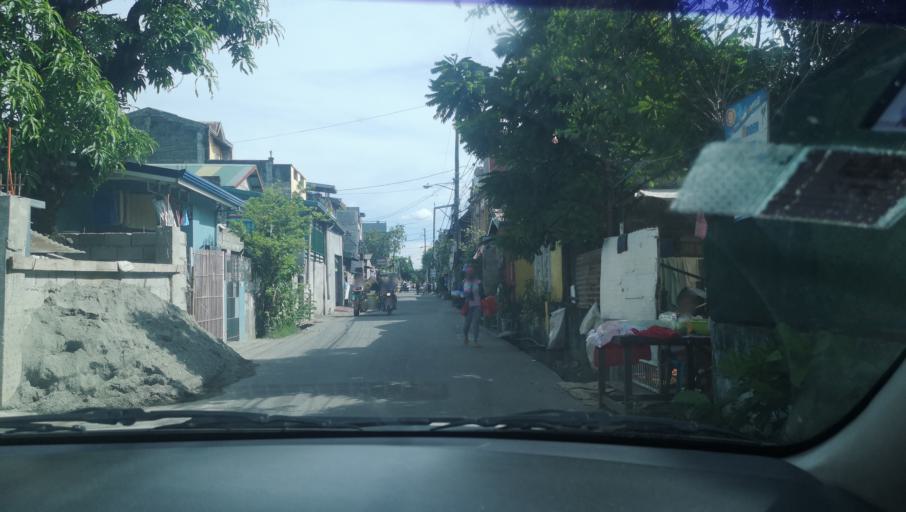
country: PH
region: Calabarzon
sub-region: Province of Rizal
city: San Mateo
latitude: 14.6761
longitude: 121.1151
